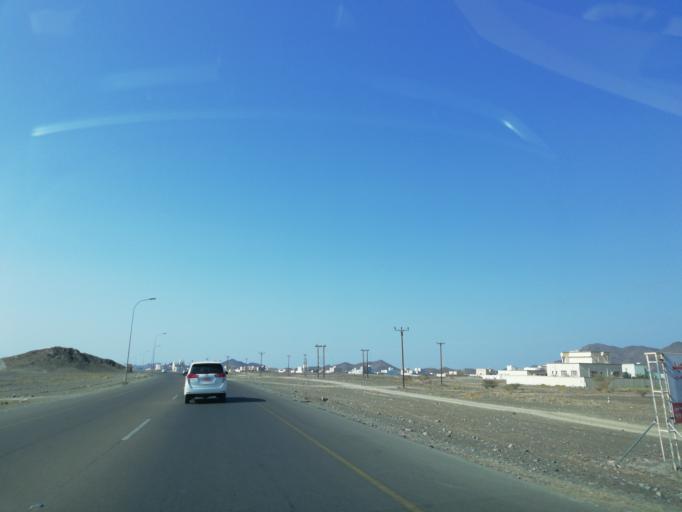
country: OM
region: Ash Sharqiyah
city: Ibra'
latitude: 22.7781
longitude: 58.1427
